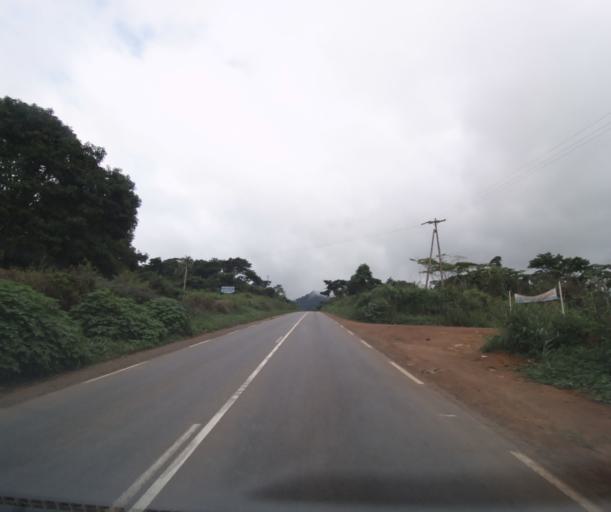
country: CM
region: Centre
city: Mbankomo
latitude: 3.7999
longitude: 11.3498
